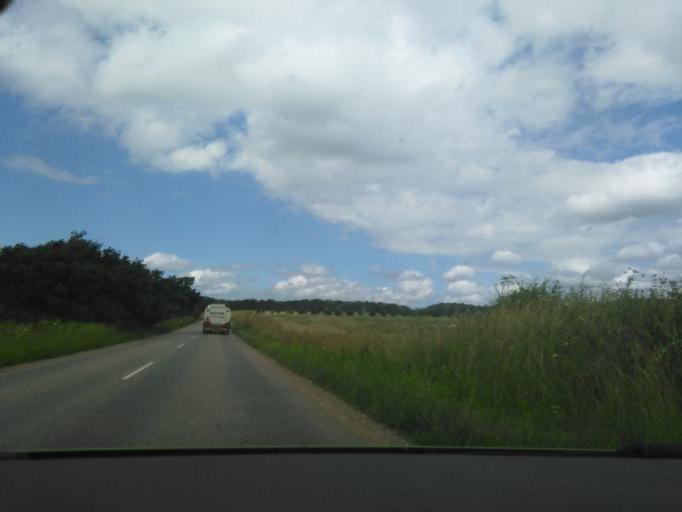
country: DK
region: Zealand
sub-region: Kalundborg Kommune
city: Hong
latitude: 55.5684
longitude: 11.3172
